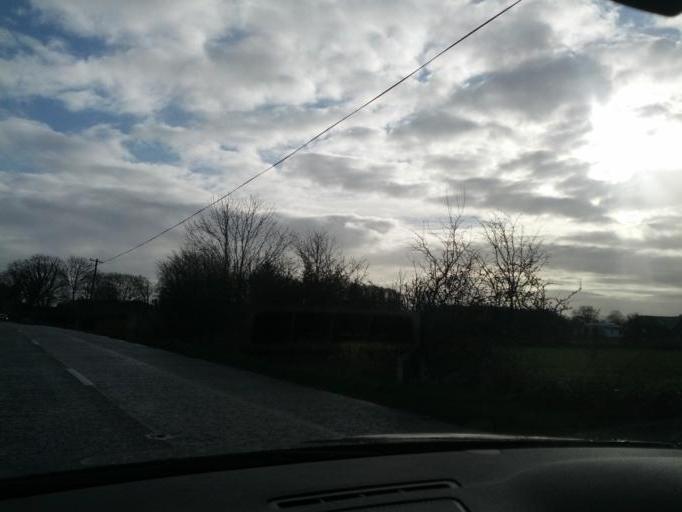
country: IE
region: Connaught
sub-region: County Galway
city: Athenry
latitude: 53.3287
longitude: -8.8276
